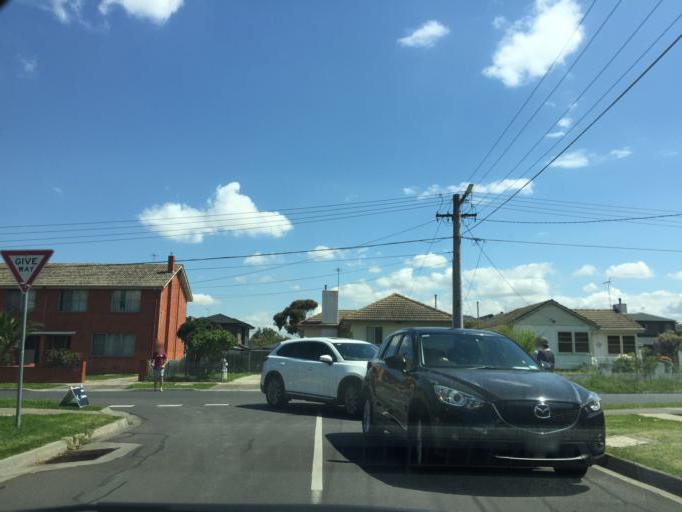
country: AU
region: Victoria
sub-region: Maribyrnong
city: West Footscray
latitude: -37.7891
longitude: 144.8756
